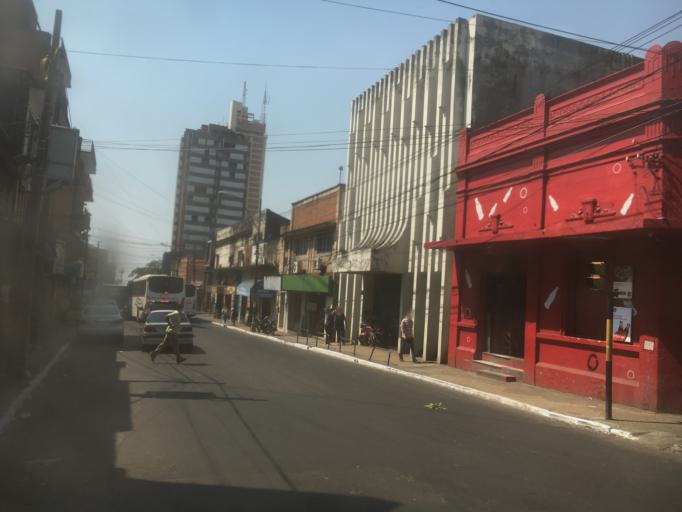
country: PY
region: Asuncion
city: Asuncion
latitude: -25.2900
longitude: -57.6256
